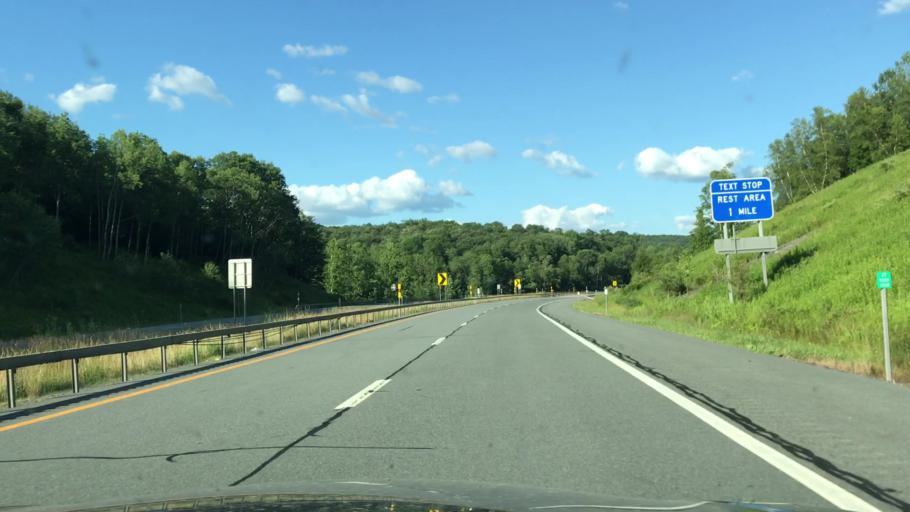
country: US
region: New York
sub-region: Sullivan County
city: Livingston Manor
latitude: 41.9254
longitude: -74.8886
